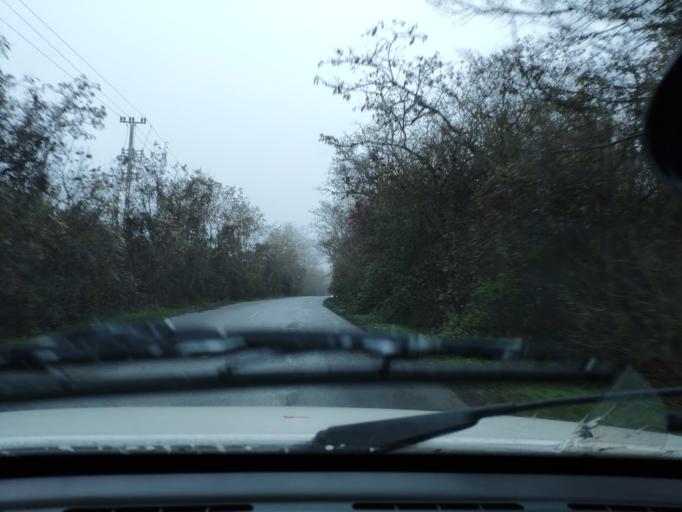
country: HU
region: Pest
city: Telki
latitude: 47.5354
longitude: 18.8425
